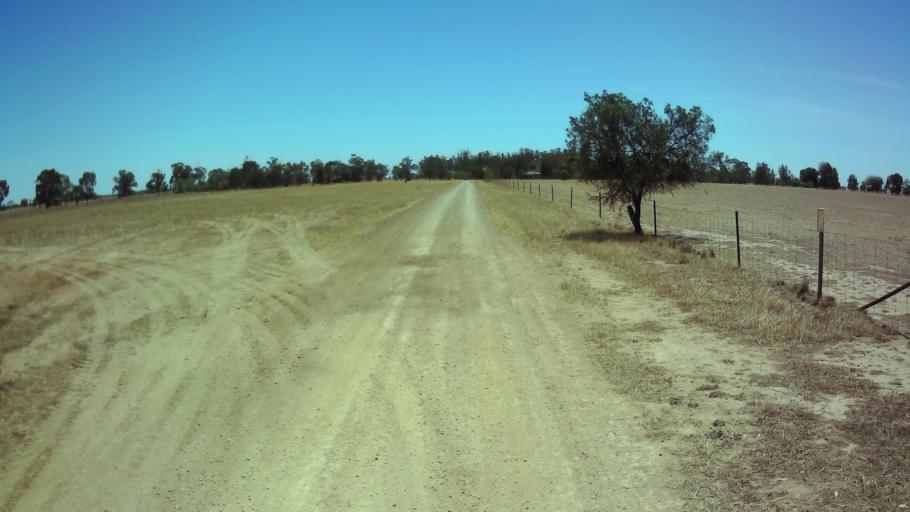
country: AU
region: New South Wales
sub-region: Weddin
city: Grenfell
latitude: -33.9980
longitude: 147.7352
